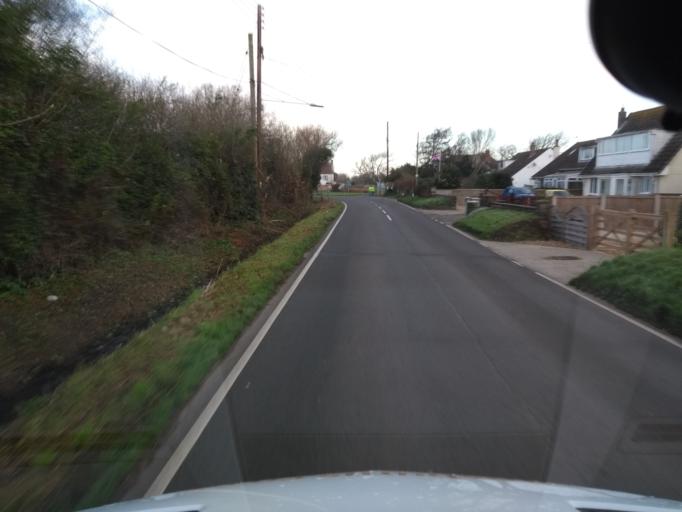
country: GB
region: England
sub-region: Somerset
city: Burnham-on-Sea
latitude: 51.2736
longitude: -3.0121
